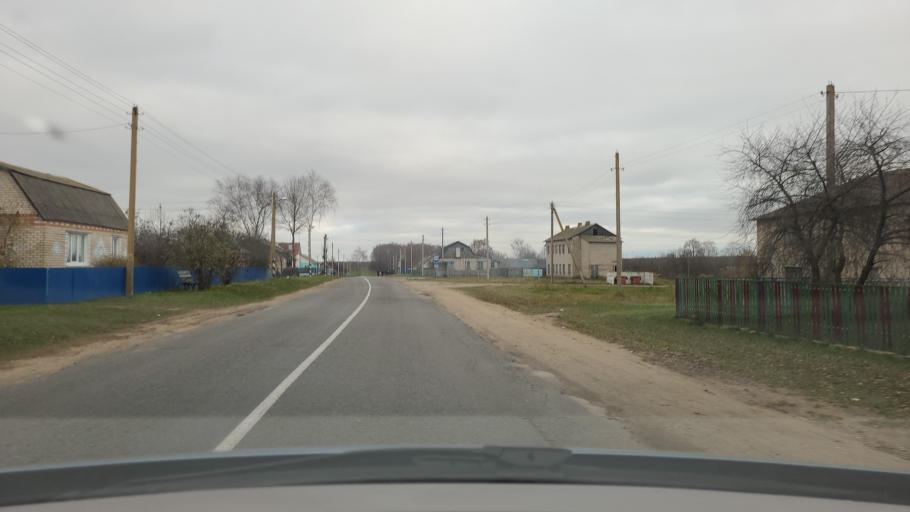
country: BY
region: Minsk
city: Khalopyenichy
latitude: 54.4700
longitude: 28.9798
